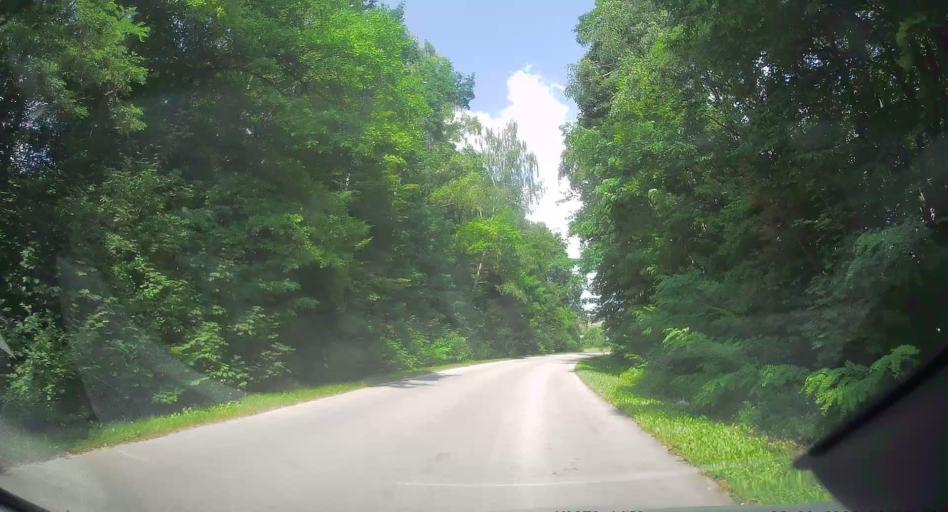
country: PL
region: Swietokrzyskie
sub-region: Powiat kielecki
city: Checiny
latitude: 50.7901
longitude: 20.4510
